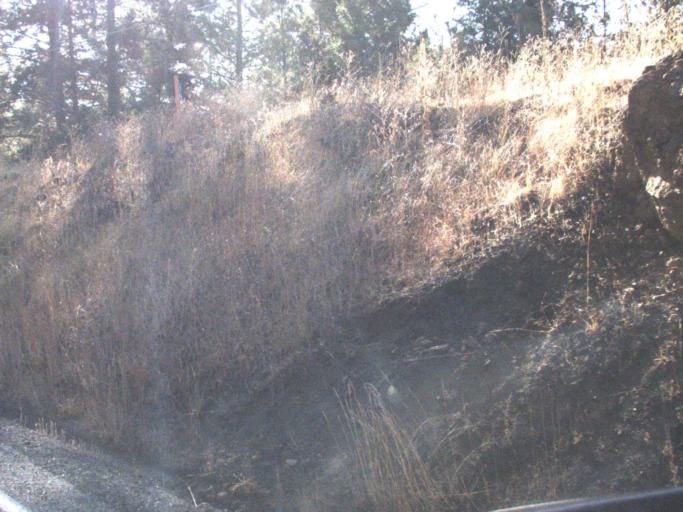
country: US
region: Washington
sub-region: Ferry County
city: Republic
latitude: 48.6389
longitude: -118.6795
